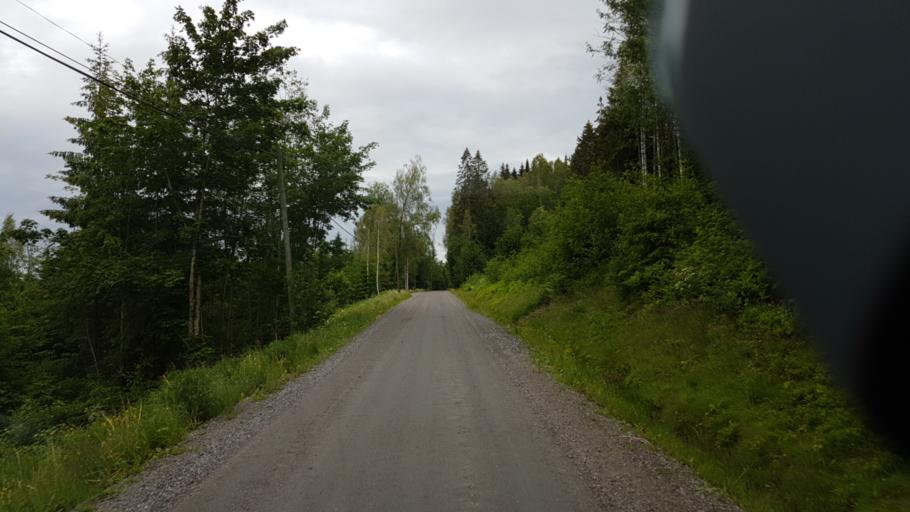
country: SE
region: Vaermland
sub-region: Eda Kommun
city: Amotfors
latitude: 59.7427
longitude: 12.2768
